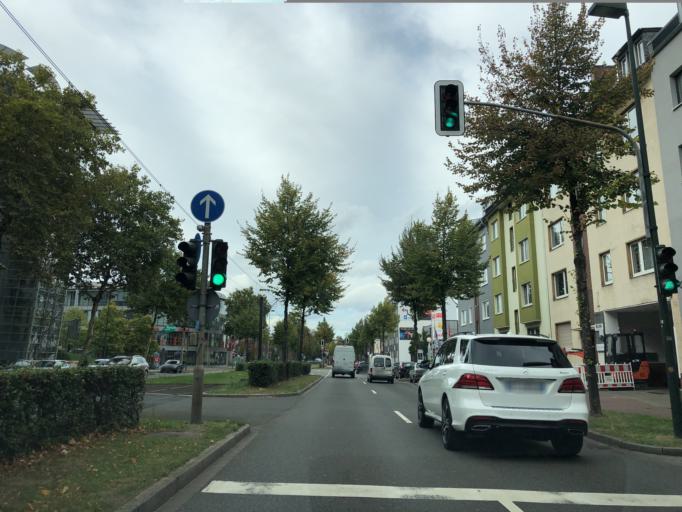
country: DE
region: North Rhine-Westphalia
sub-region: Regierungsbezirk Dusseldorf
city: Dusseldorf
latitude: 51.1954
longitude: 6.8134
